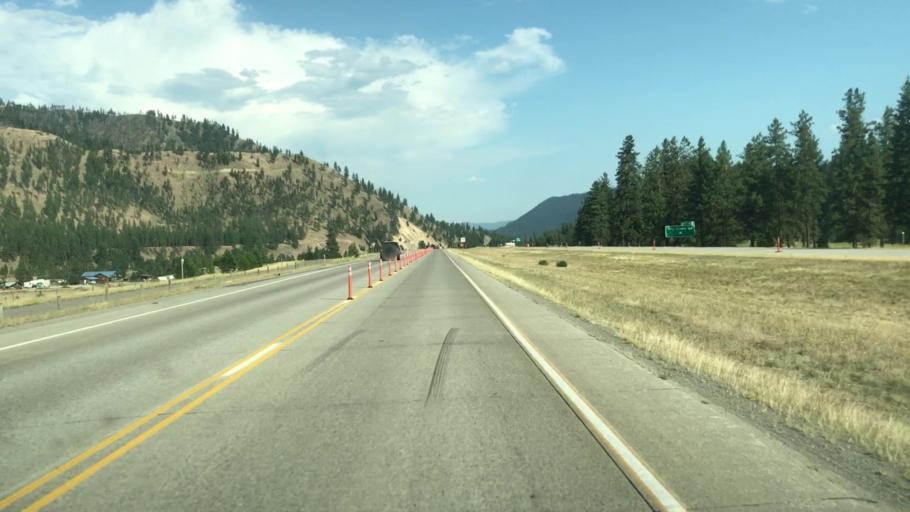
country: US
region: Montana
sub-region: Mineral County
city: Superior
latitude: 47.2295
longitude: -114.9762
